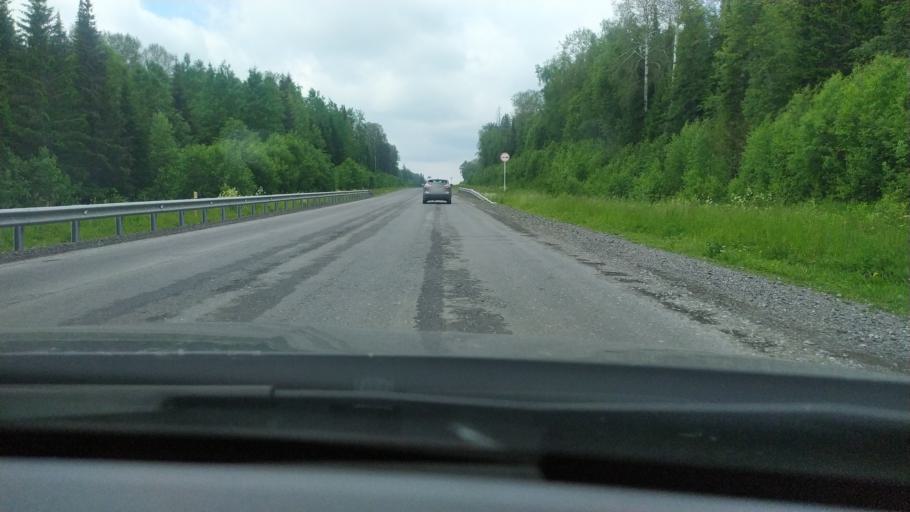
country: RU
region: Perm
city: Kalino
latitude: 58.2714
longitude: 57.3752
